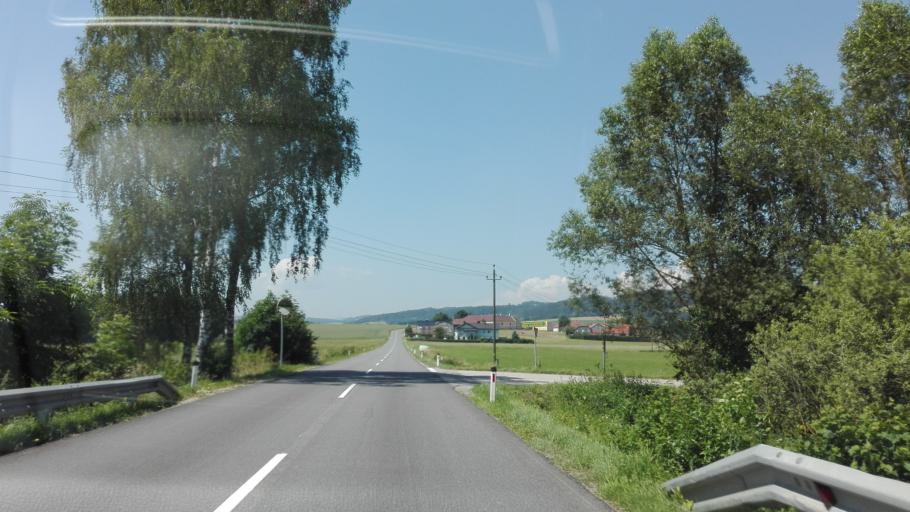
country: AT
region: Upper Austria
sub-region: Politischer Bezirk Grieskirchen
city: Grieskirchen
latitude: 48.3535
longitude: 13.8661
